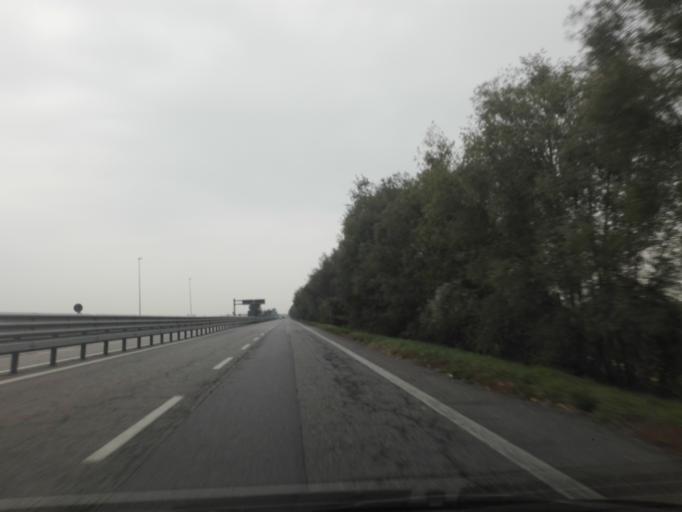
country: IT
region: Veneto
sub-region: Provincia di Verona
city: Isola Rizza
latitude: 45.2735
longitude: 11.2176
